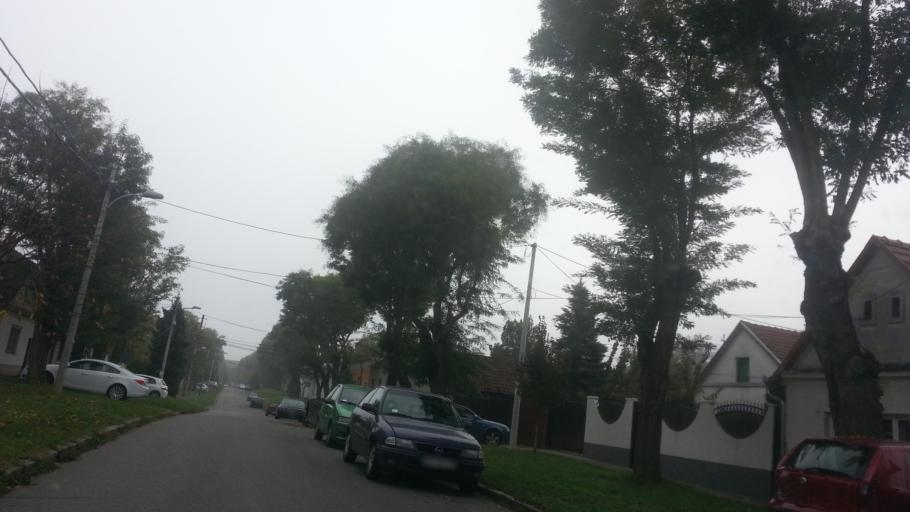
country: RS
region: Central Serbia
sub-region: Belgrade
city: Zemun
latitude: 44.8526
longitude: 20.3982
